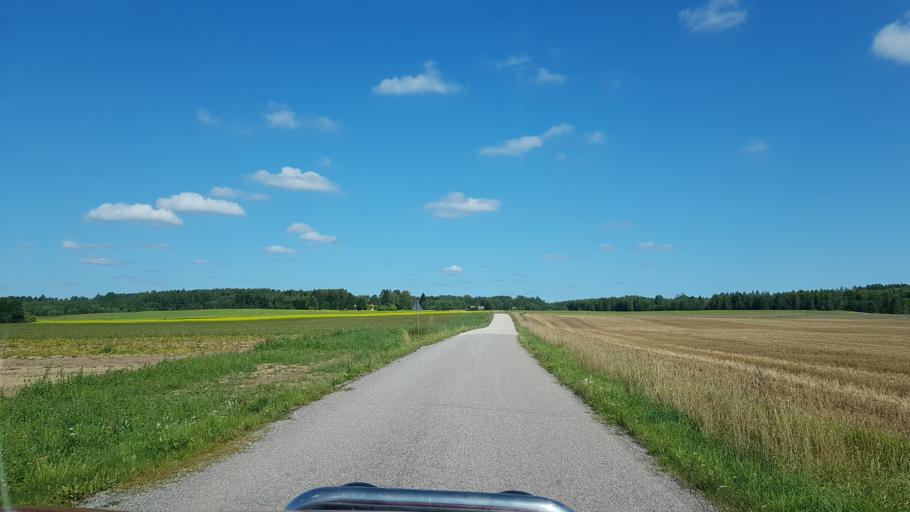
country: RU
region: Pskov
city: Pechory
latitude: 57.7118
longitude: 27.3953
